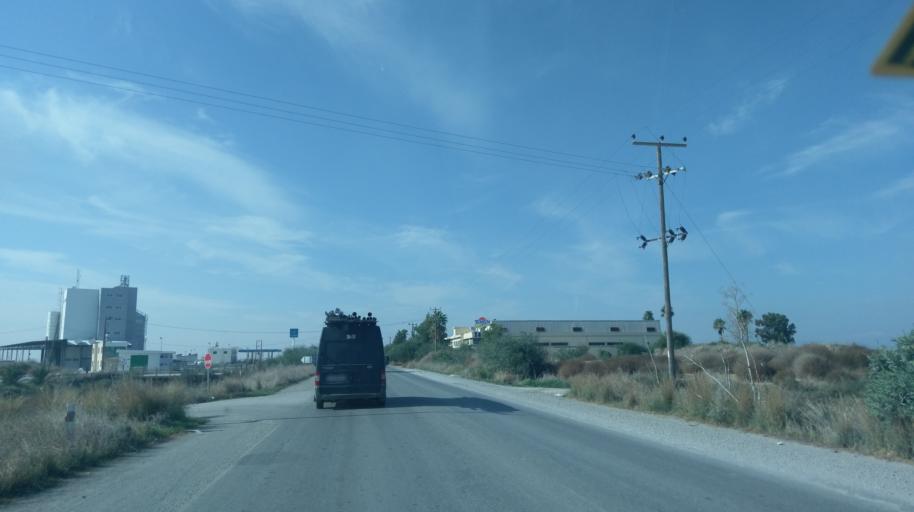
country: CY
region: Ammochostos
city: Acheritou
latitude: 35.1483
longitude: 33.8775
